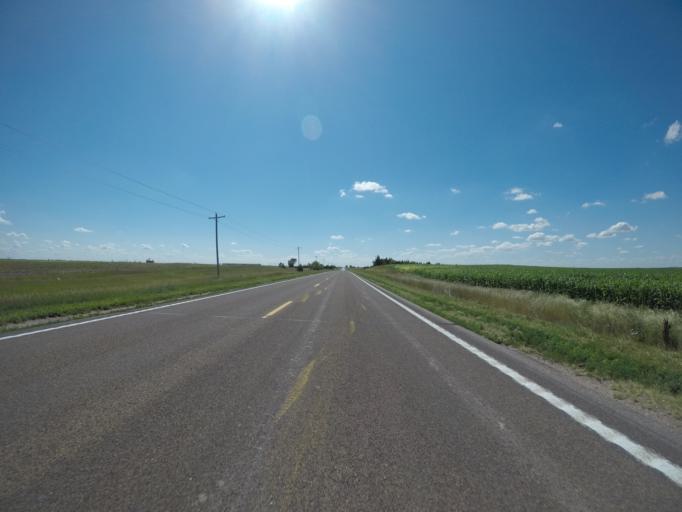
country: US
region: Nebraska
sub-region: Chase County
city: Imperial
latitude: 40.5375
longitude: -101.8322
